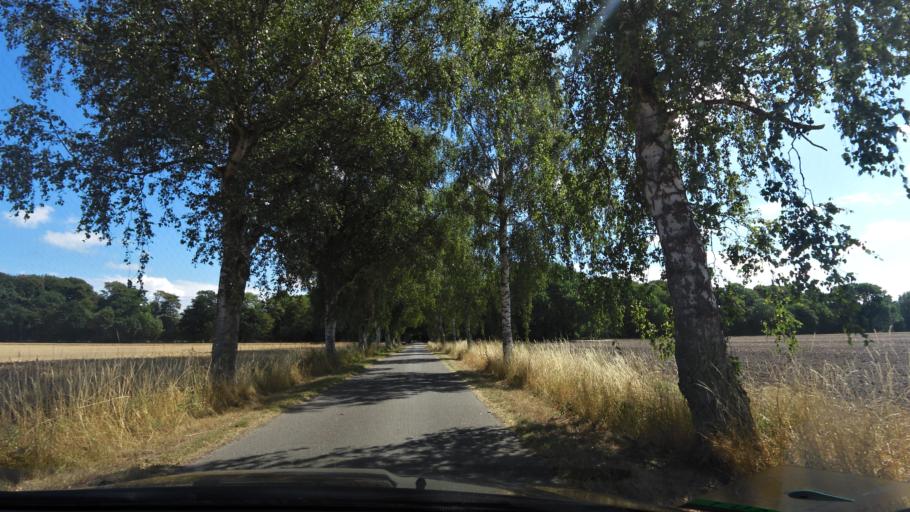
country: DK
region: South Denmark
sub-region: Nordfyns Kommune
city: Otterup
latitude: 55.5390
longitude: 10.4750
